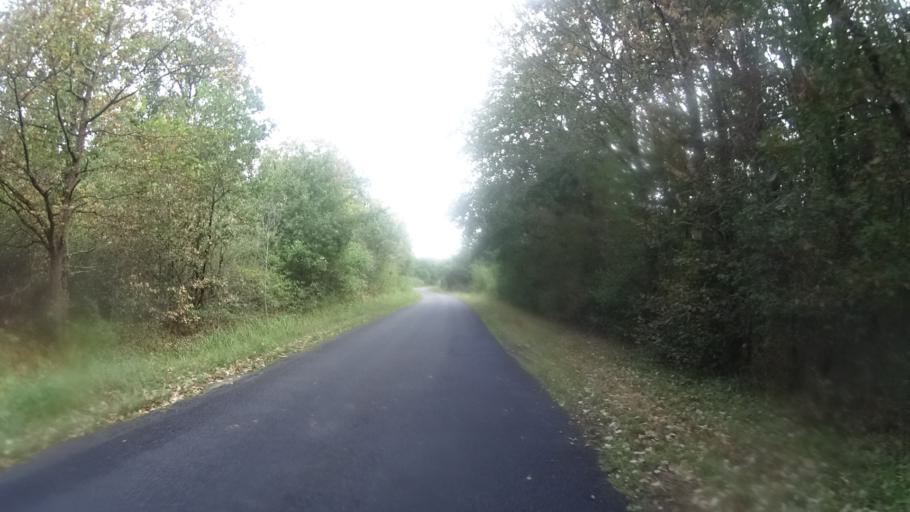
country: FR
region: Centre
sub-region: Departement du Loiret
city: Fay-aux-Loges
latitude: 47.9783
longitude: 2.1932
